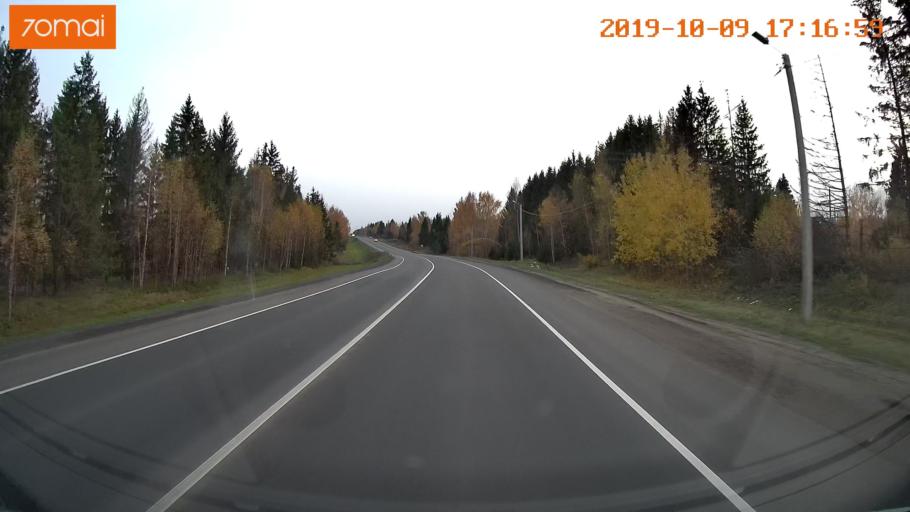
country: RU
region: Ivanovo
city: Furmanov
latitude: 57.2820
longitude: 41.1594
